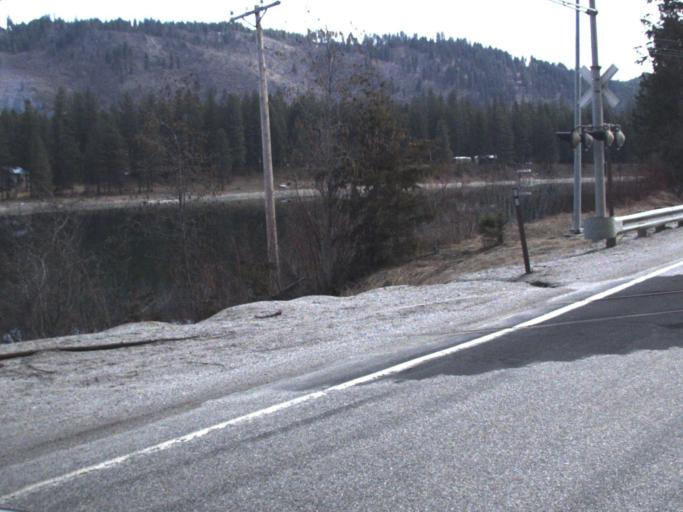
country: US
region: Washington
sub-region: Stevens County
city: Chewelah
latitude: 48.5577
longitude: -117.3491
